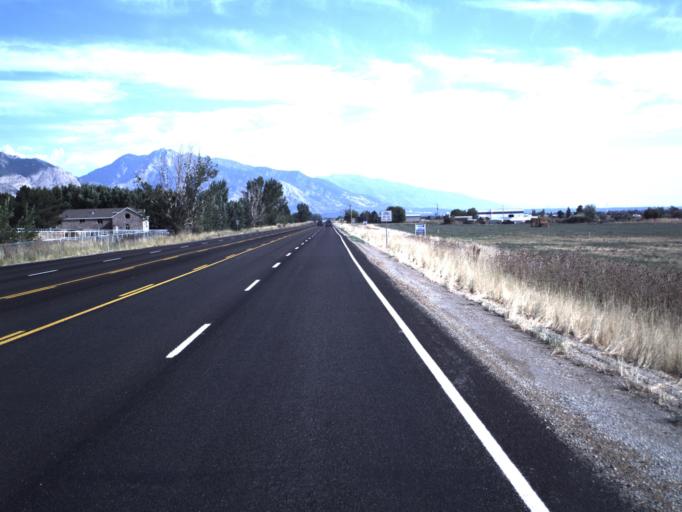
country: US
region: Utah
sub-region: Box Elder County
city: South Willard
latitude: 41.3324
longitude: -112.0252
